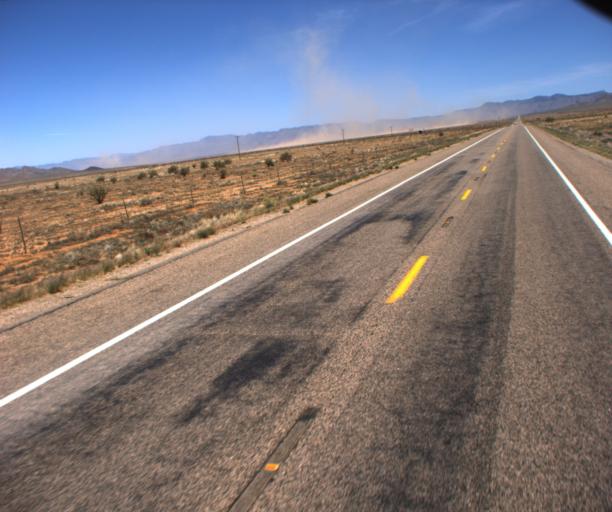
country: US
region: Arizona
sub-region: Mohave County
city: New Kingman-Butler
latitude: 35.3213
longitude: -113.9112
